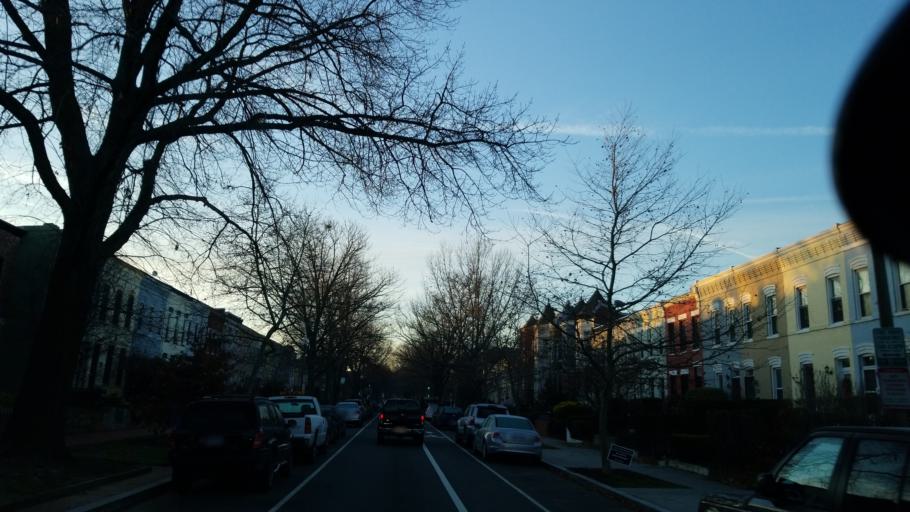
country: US
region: Washington, D.C.
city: Washington, D.C.
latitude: 38.8933
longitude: -76.9855
